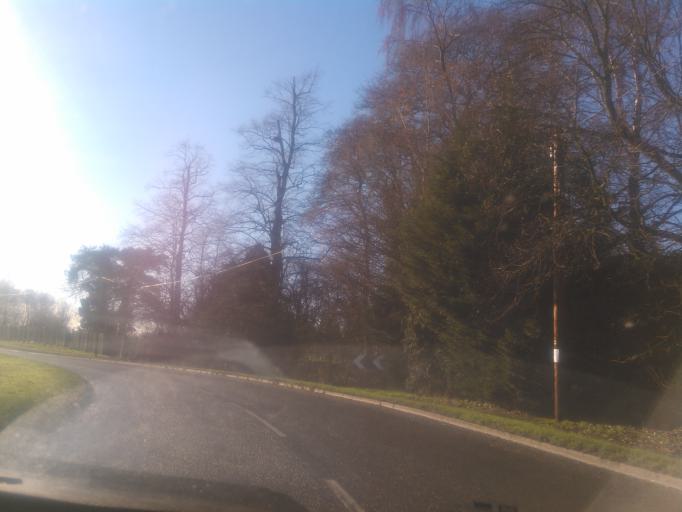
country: GB
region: England
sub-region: Shropshire
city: Wem
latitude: 52.8637
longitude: -2.7016
